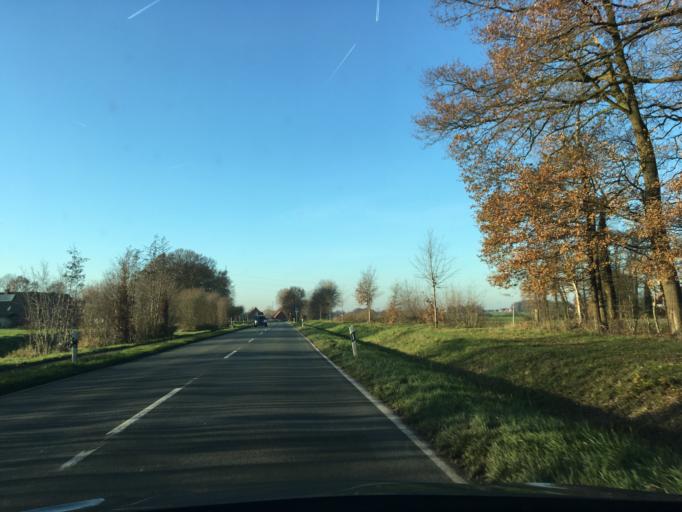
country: DE
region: North Rhine-Westphalia
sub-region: Regierungsbezirk Munster
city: Ahaus
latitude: 52.1173
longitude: 6.9378
